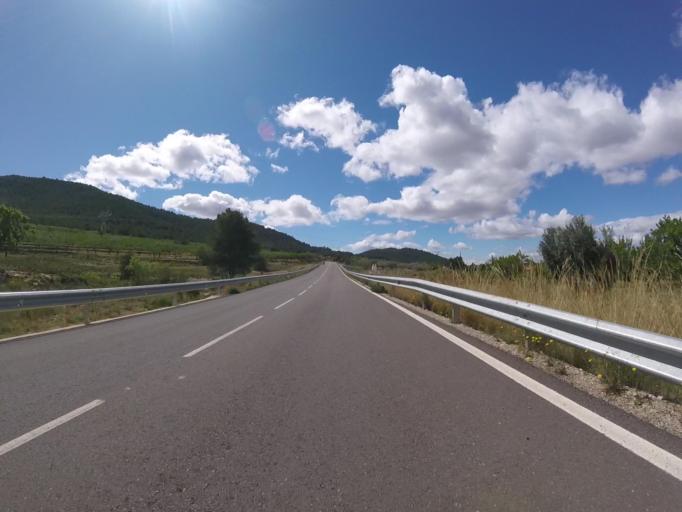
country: ES
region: Valencia
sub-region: Provincia de Castello
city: Culla
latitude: 40.2869
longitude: -0.1136
